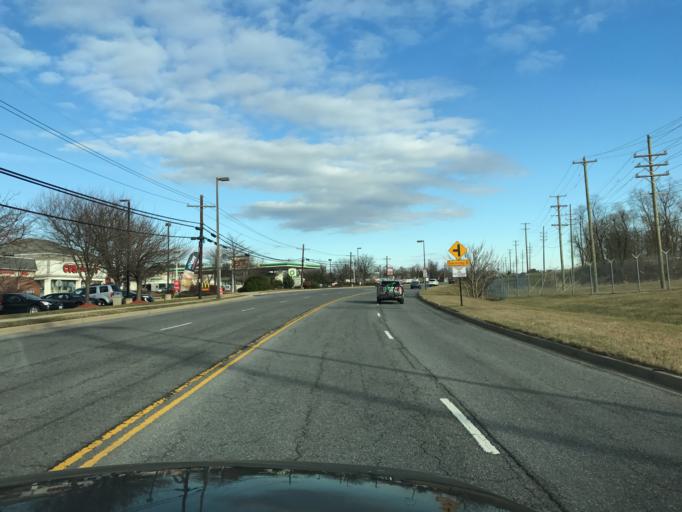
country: US
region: Maryland
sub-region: Frederick County
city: Clover Hill
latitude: 39.4394
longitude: -77.4375
